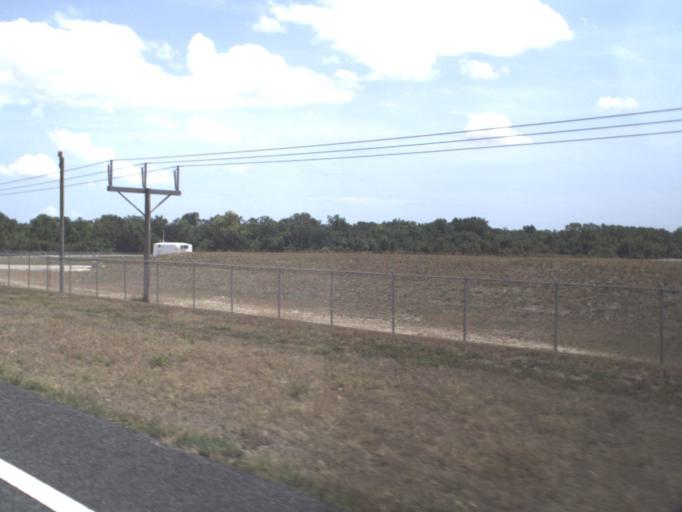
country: US
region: Florida
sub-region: Brevard County
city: Port Saint John
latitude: 28.5277
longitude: -80.7988
